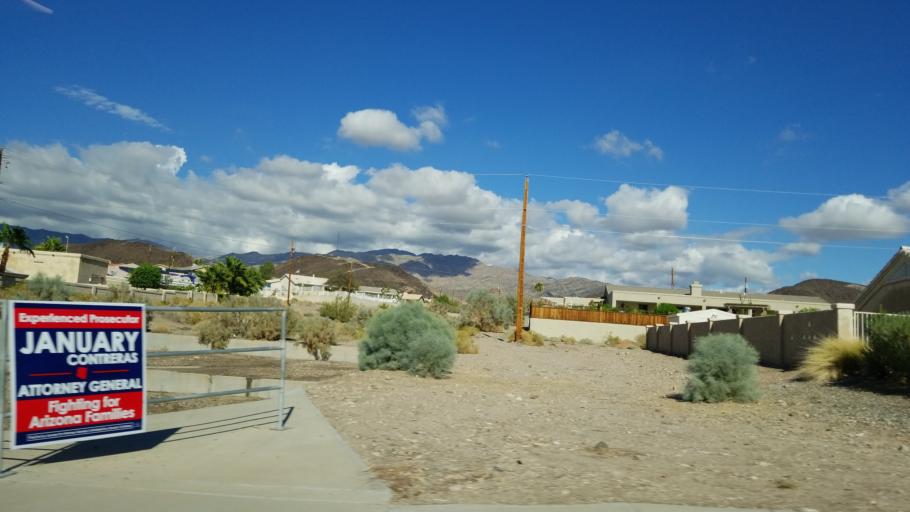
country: US
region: Arizona
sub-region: Mohave County
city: Lake Havasu City
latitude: 34.4829
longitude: -114.2678
